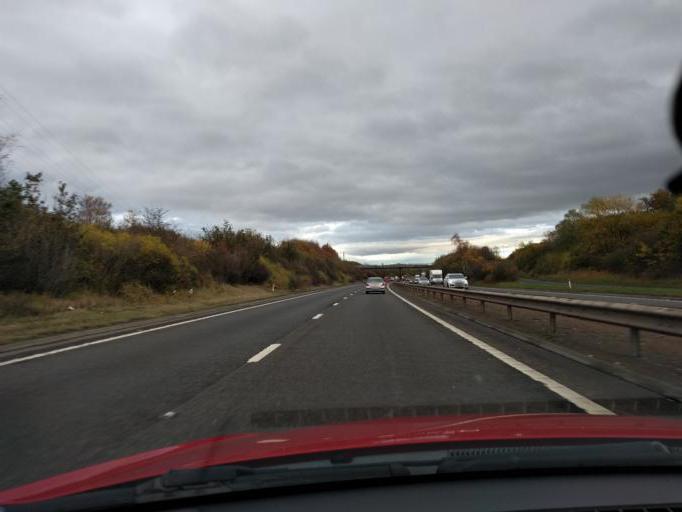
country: GB
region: Scotland
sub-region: Midlothian
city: Bonnyrigg
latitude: 55.8982
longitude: -3.1160
